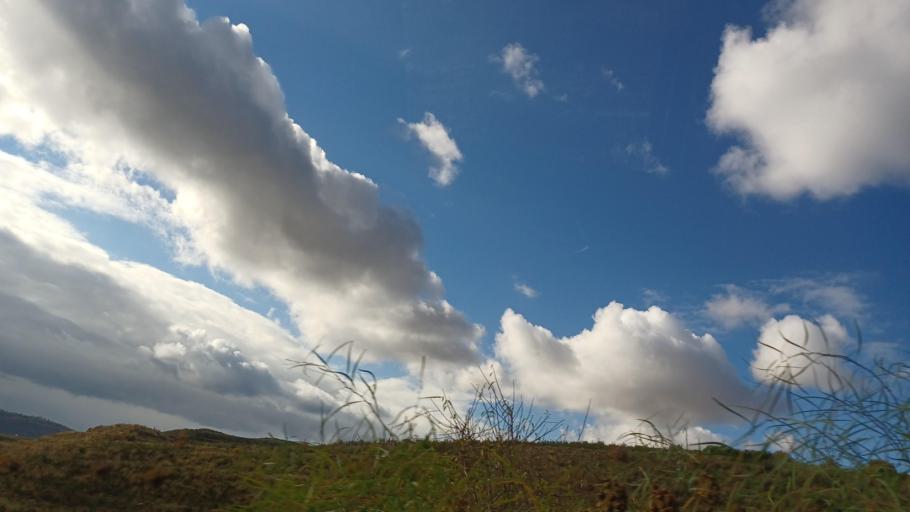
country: CY
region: Limassol
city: Pachna
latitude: 34.7906
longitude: 32.8238
